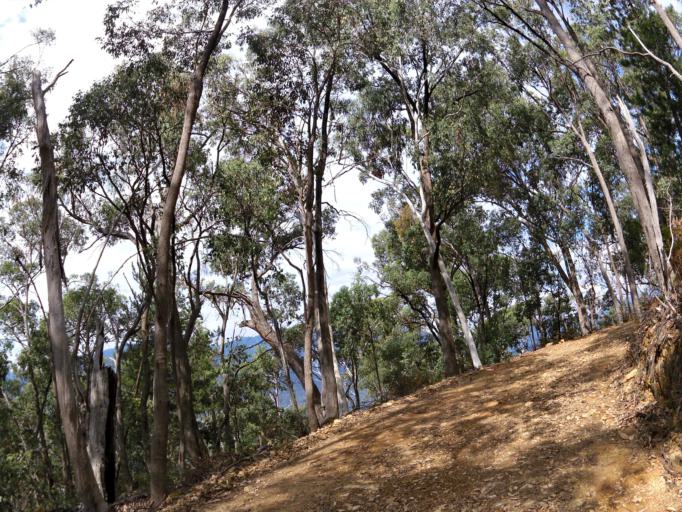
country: AU
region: Victoria
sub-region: Alpine
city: Mount Beauty
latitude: -36.7747
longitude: 147.0157
